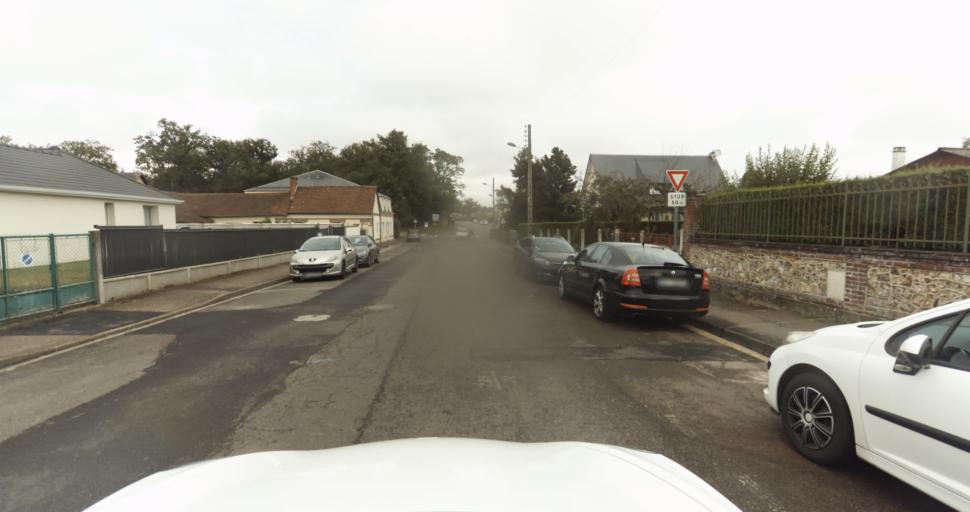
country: FR
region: Haute-Normandie
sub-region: Departement de l'Eure
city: Evreux
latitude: 49.0319
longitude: 1.1355
